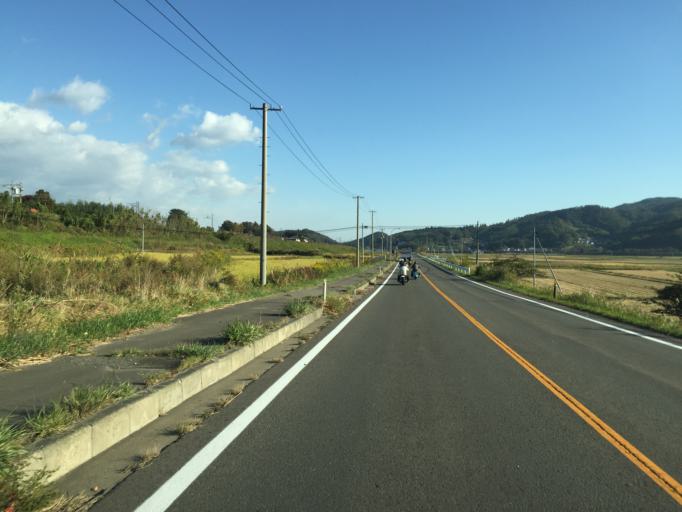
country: JP
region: Fukushima
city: Yanagawamachi-saiwaicho
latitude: 37.9225
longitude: 140.5994
